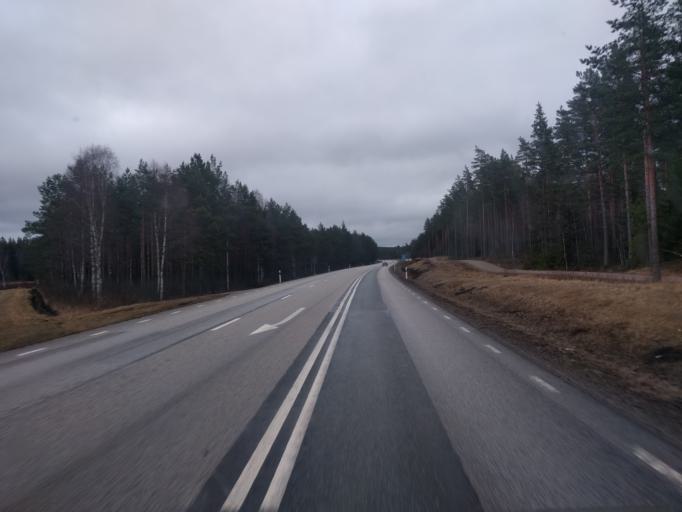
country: SE
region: Joenkoeping
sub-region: Eksjo Kommun
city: Haljarp
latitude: 57.6354
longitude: 15.3779
